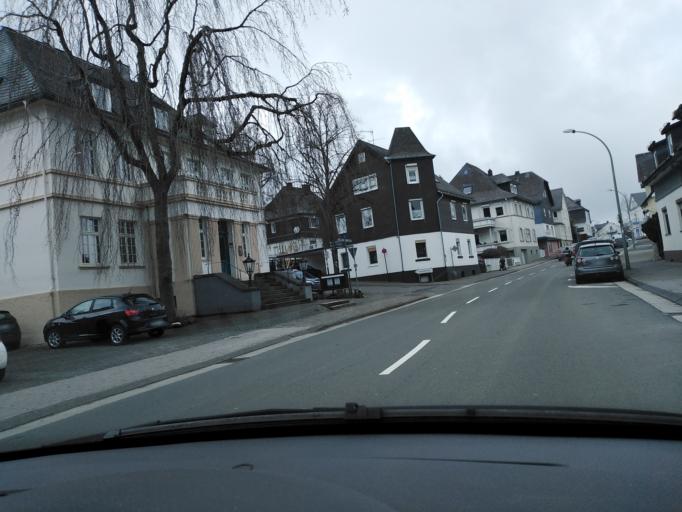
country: DE
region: North Rhine-Westphalia
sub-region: Regierungsbezirk Arnsberg
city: Brilon
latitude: 51.3938
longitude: 8.5730
